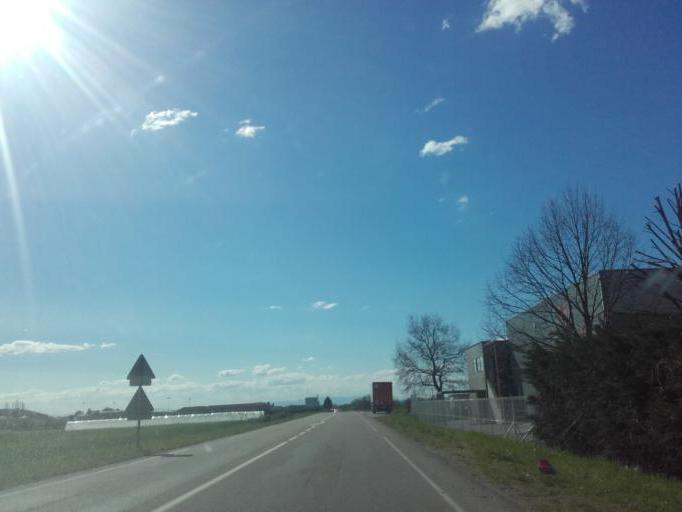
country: FR
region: Rhone-Alpes
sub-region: Departement de l'Isere
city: Saint-Etienne-de-Saint-Geoirs
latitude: 45.3472
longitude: 5.3514
